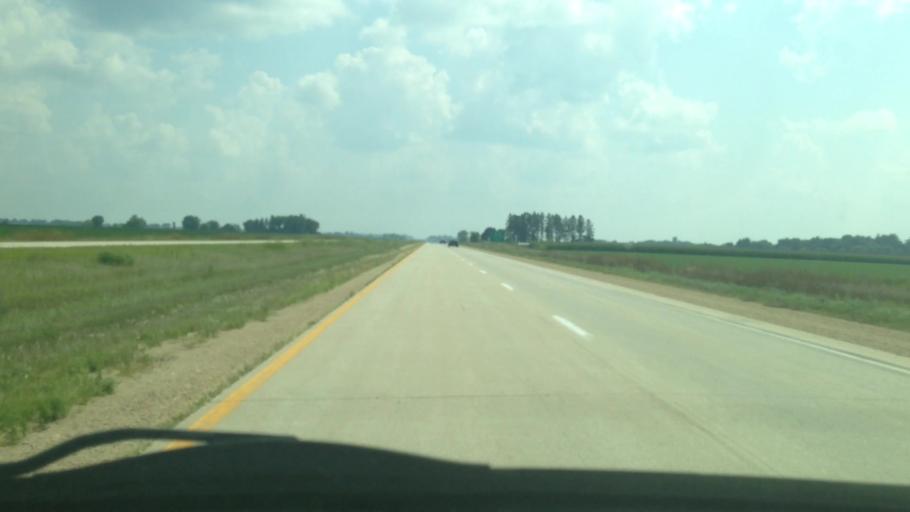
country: US
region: Iowa
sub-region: Chickasaw County
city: New Hampton
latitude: 42.9878
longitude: -92.3177
